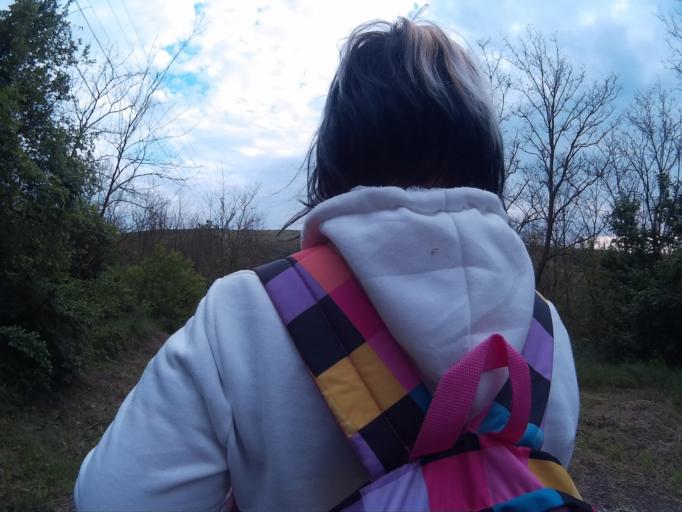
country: HU
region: Zala
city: Cserszegtomaj
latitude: 46.8301
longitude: 17.1993
